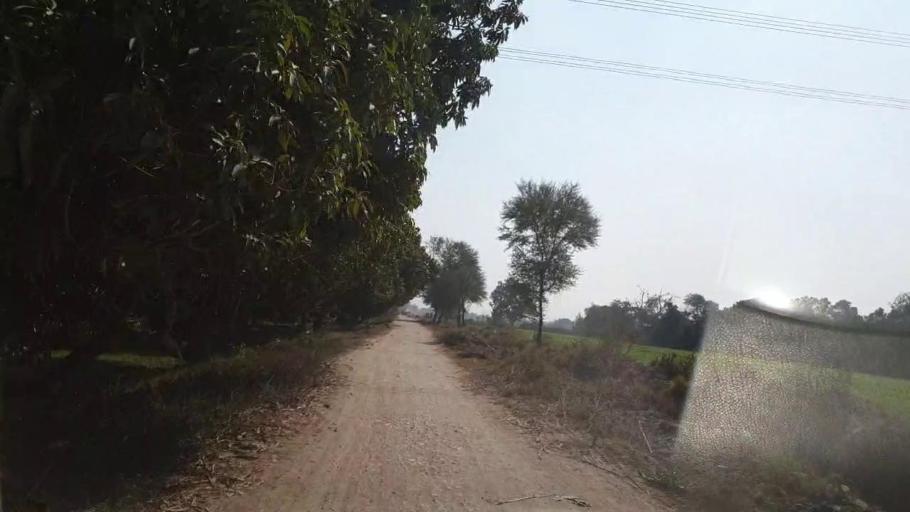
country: PK
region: Sindh
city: Matiari
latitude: 25.5135
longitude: 68.4601
